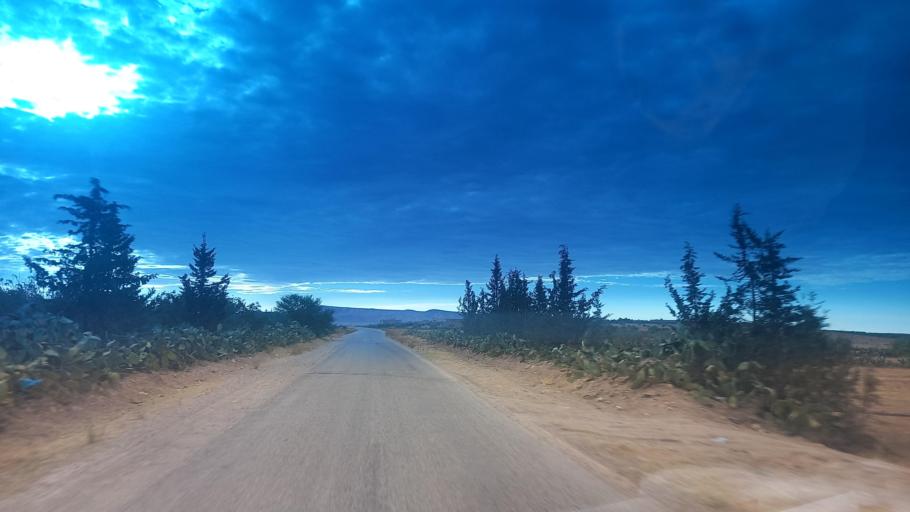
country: TN
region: Al Qasrayn
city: Sbiba
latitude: 35.3839
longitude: 9.0395
